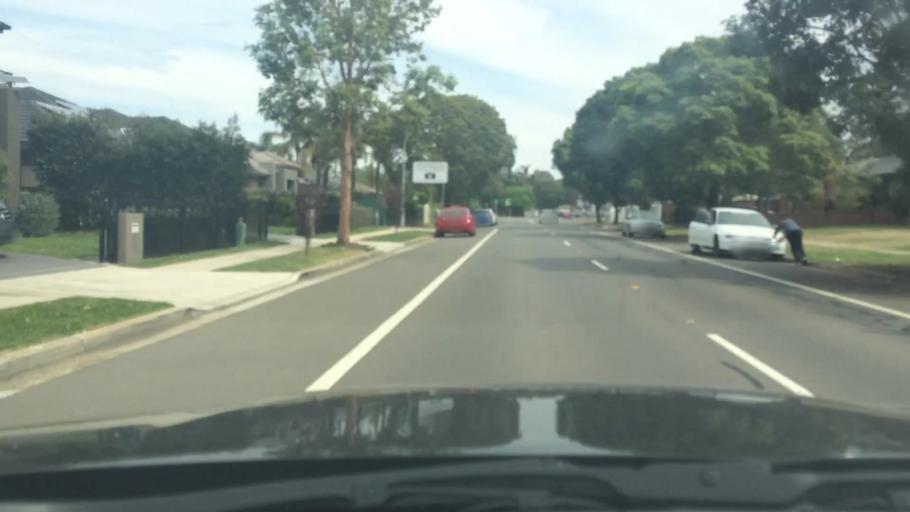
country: AU
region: New South Wales
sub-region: Fairfield
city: Cabramatta West
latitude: -33.8647
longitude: 150.8977
